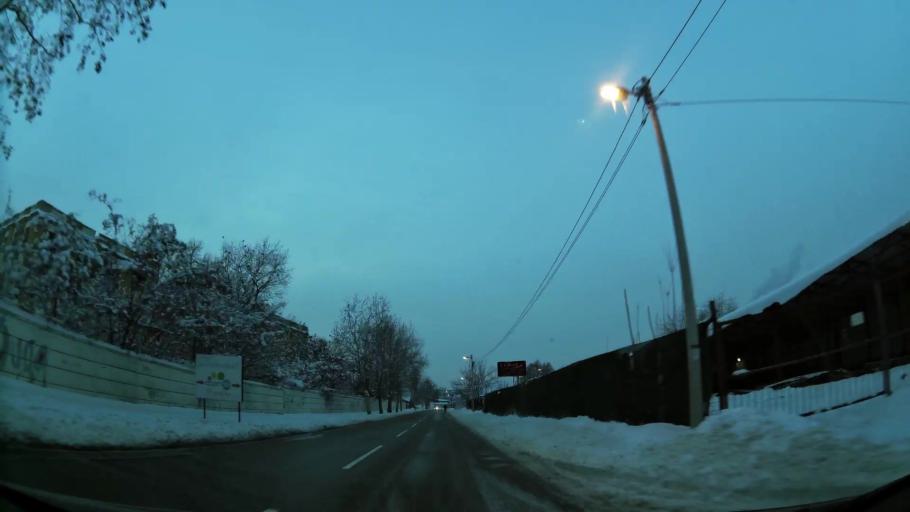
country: RS
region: Central Serbia
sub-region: Belgrade
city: Stari Grad
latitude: 44.8214
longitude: 20.4793
